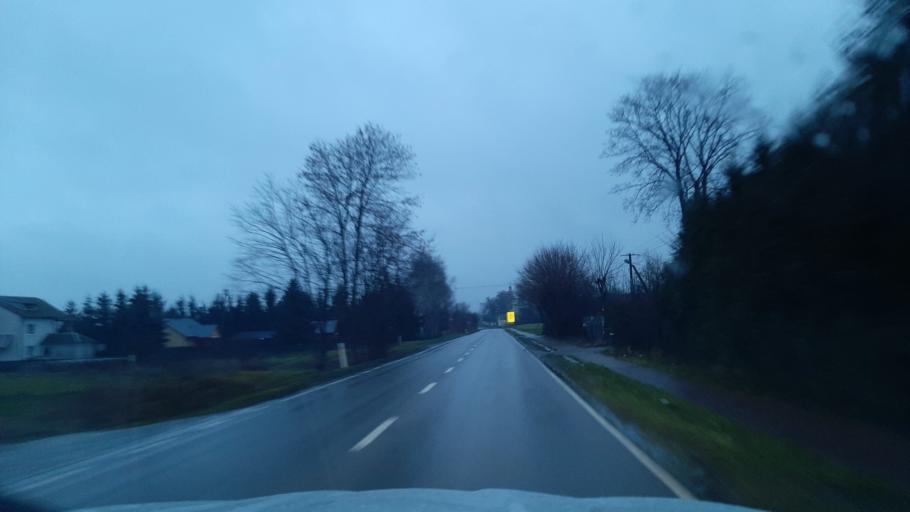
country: PL
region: Lublin Voivodeship
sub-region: Powiat lubelski
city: Jastkow
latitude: 51.3612
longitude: 22.4626
